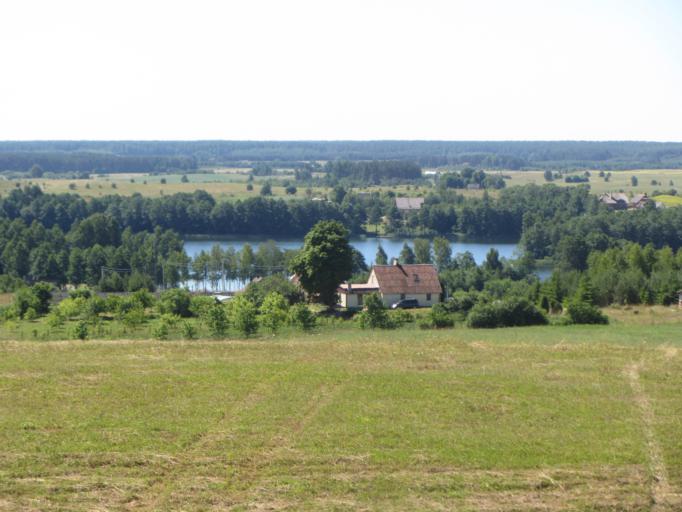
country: LT
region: Vilnius County
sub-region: Vilniaus Rajonas
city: Vievis
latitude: 54.6455
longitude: 24.8007
